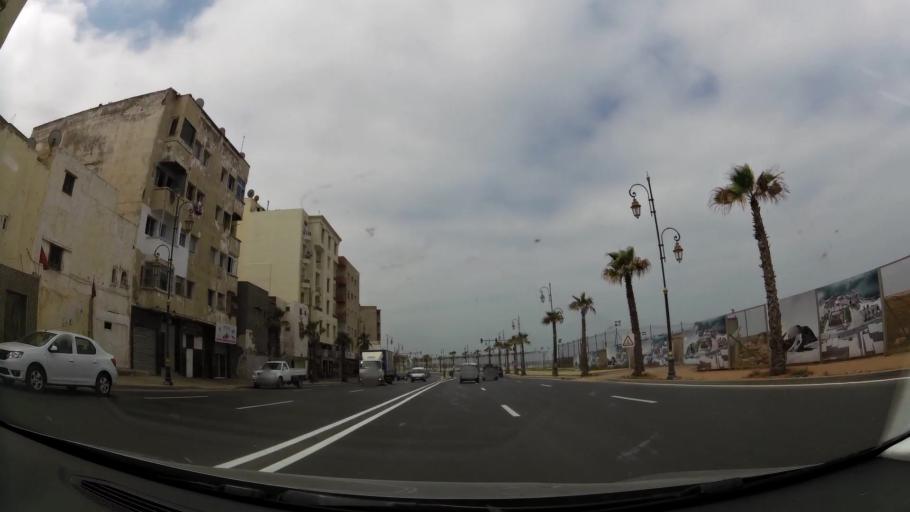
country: MA
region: Rabat-Sale-Zemmour-Zaer
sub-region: Rabat
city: Rabat
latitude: 34.0247
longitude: -6.8508
